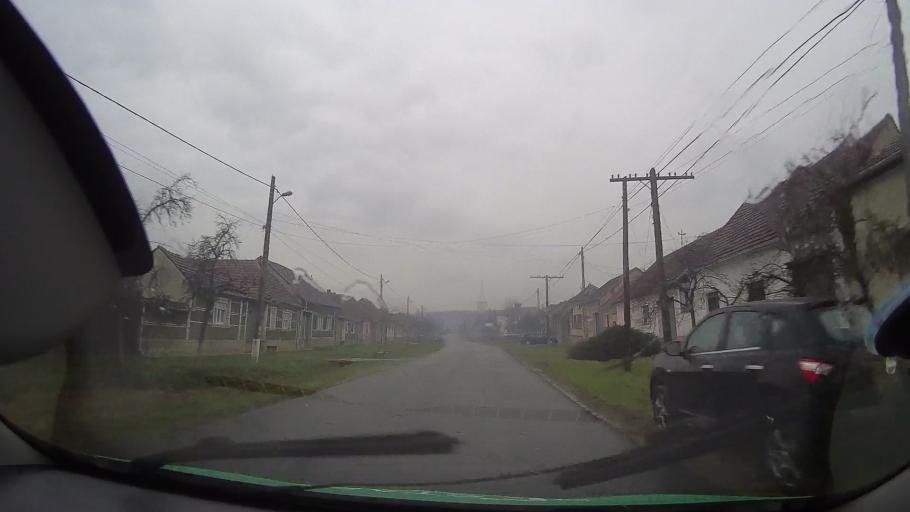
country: RO
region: Bihor
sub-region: Comuna Uileacu de Beius
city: Uileacu de Beius
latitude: 46.6836
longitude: 22.2225
